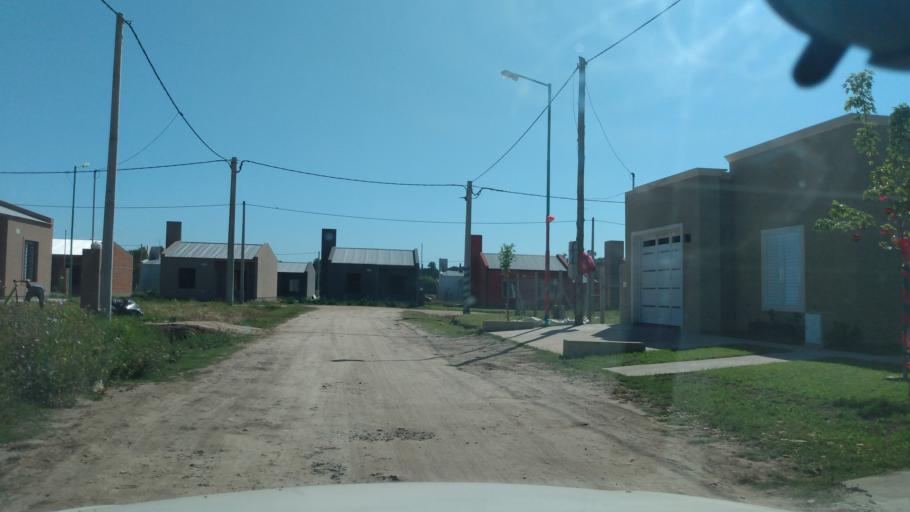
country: AR
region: Buenos Aires
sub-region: Partido de Lujan
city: Lujan
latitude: -34.5533
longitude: -59.1376
